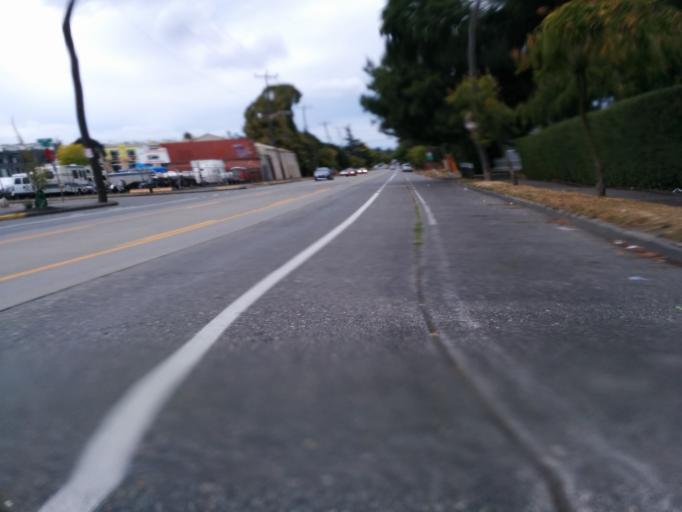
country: US
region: Washington
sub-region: King County
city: Seattle
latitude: 47.6633
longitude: -122.3662
